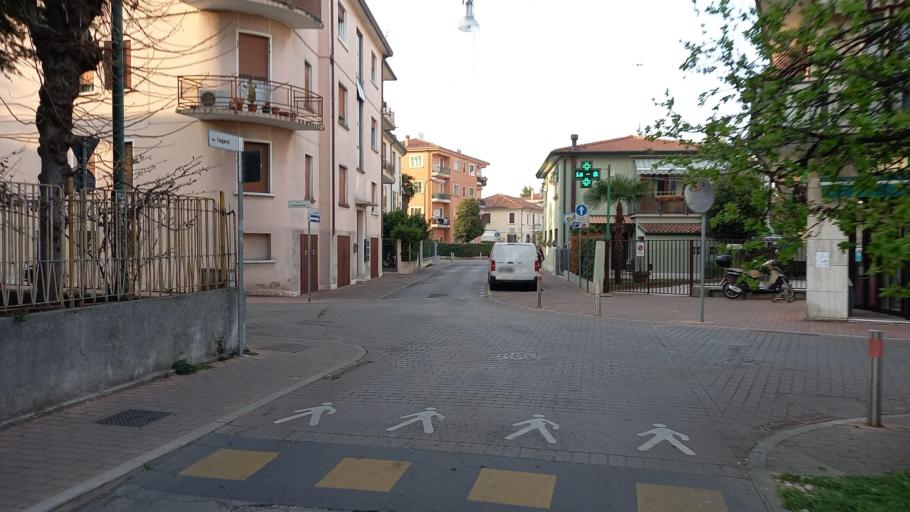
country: IT
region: Veneto
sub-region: Provincia di Venezia
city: Mestre
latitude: 45.4855
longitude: 12.2292
